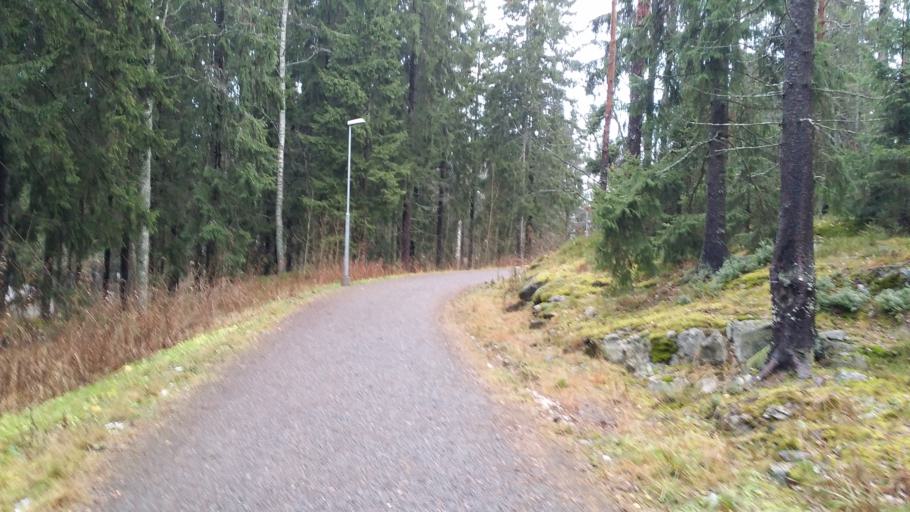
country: FI
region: Pirkanmaa
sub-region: Tampere
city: Pirkkala
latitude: 61.5048
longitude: 23.6370
